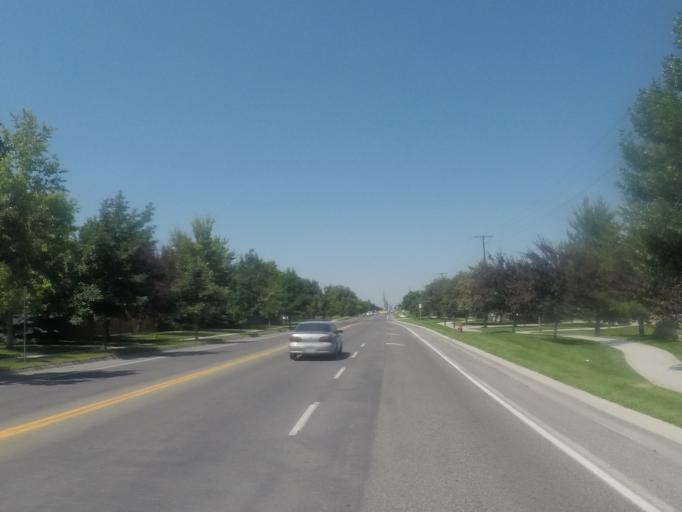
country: US
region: Montana
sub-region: Gallatin County
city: Bozeman
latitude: 45.6930
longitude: -111.0654
